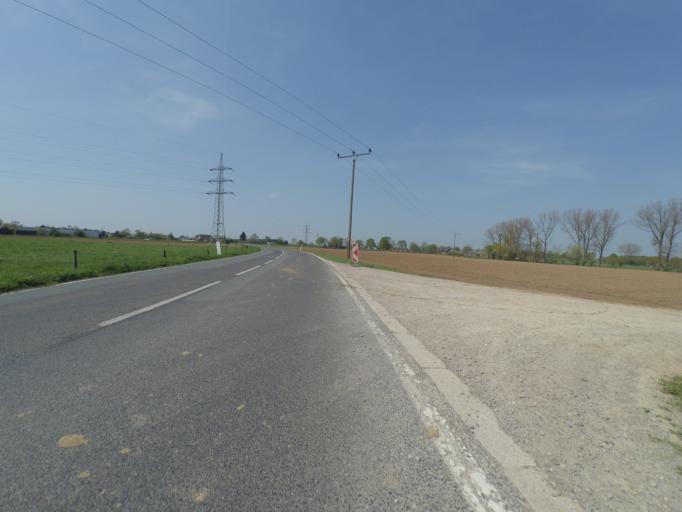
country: DE
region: North Rhine-Westphalia
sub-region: Regierungsbezirk Munster
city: Isselburg
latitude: 51.8145
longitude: 6.4212
